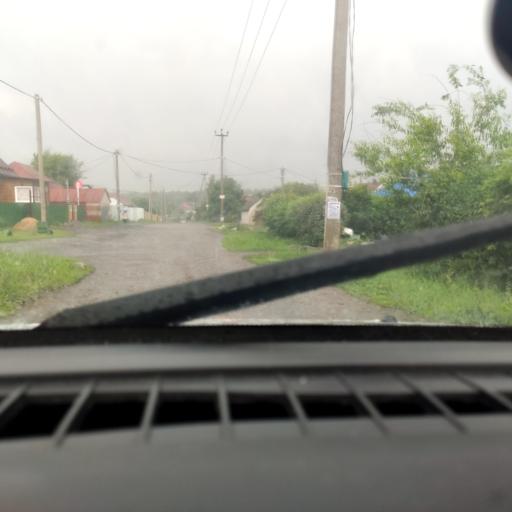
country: RU
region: Voronezj
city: Volya
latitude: 51.7526
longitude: 39.5032
